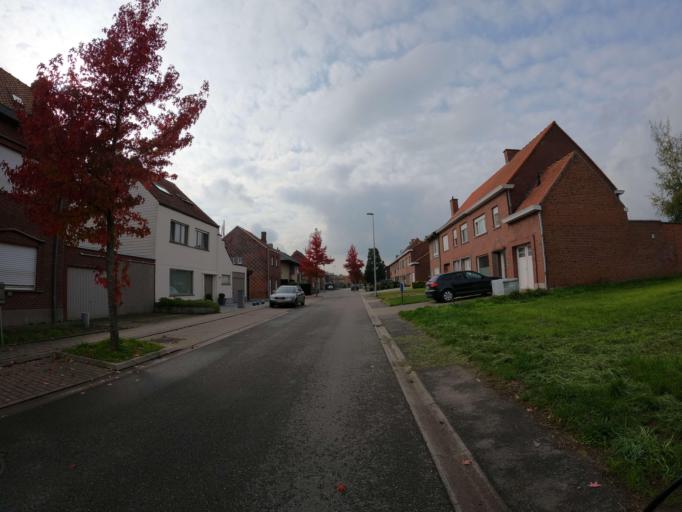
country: BE
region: Flanders
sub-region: Provincie West-Vlaanderen
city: Tielt
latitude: 51.0067
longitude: 3.3303
